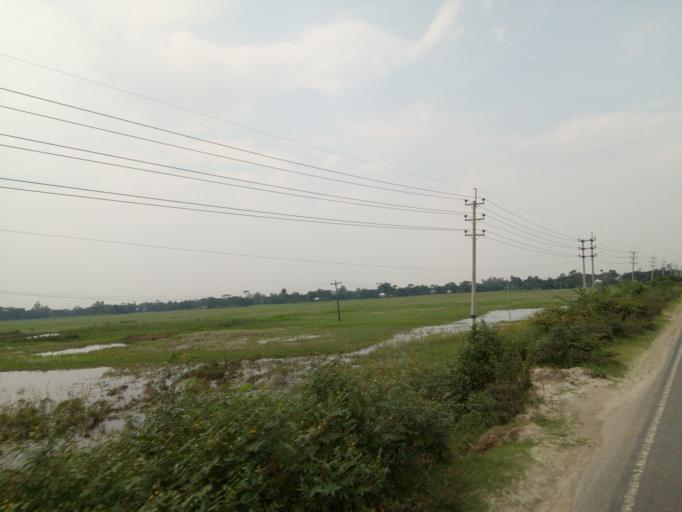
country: BD
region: Dhaka
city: Dohar
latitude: 23.5058
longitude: 90.2745
